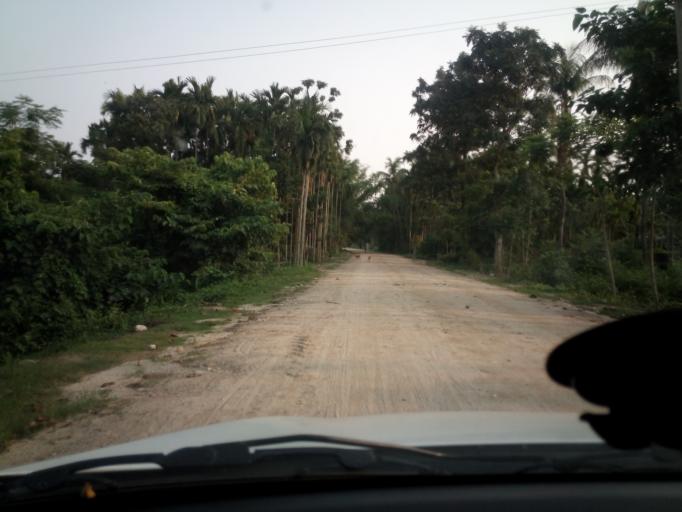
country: IN
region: Assam
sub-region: Udalguri
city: Udalguri
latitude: 26.6802
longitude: 92.0920
